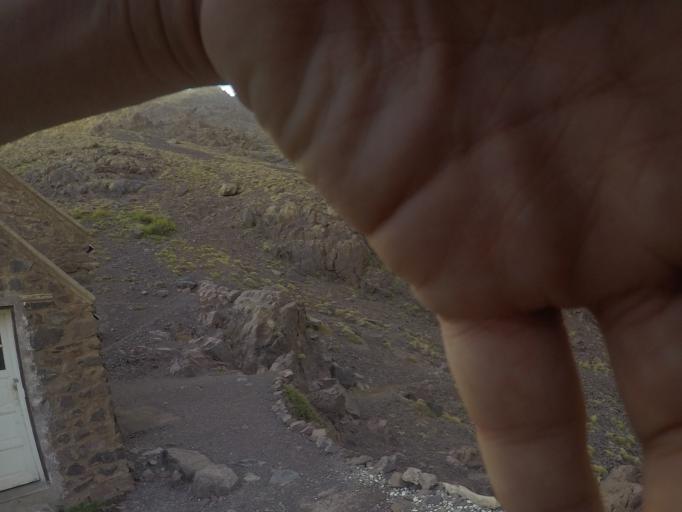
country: MA
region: Marrakech-Tensift-Al Haouz
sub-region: Al-Haouz
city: Moulay Brahim
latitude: 31.0760
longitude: -7.9623
